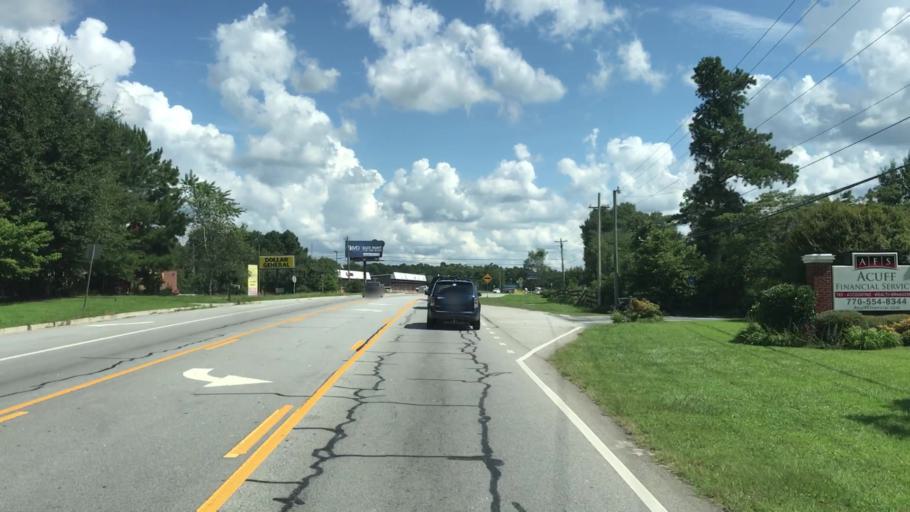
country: US
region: Georgia
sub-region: Walton County
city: Walnut Grove
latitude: 33.7822
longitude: -83.8543
